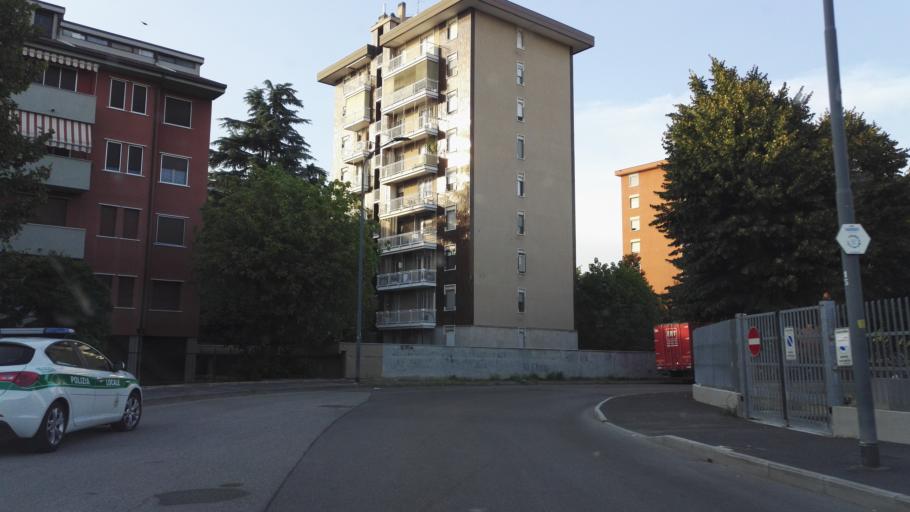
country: IT
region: Lombardy
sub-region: Citta metropolitana di Milano
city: Chiaravalle
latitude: 45.4328
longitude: 9.2495
